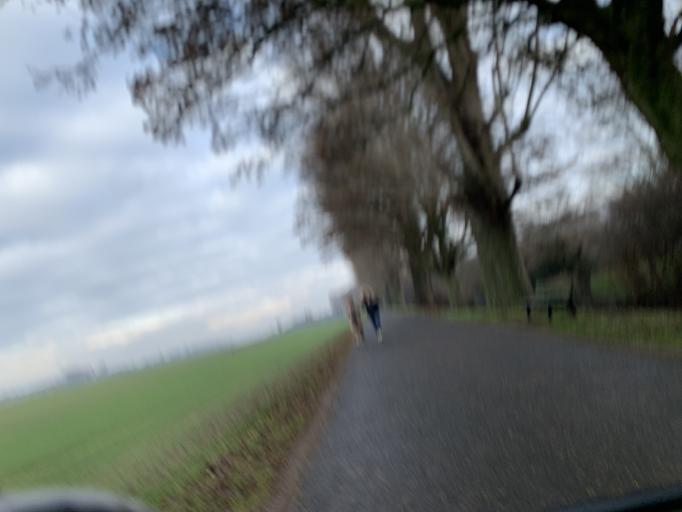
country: DE
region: North Rhine-Westphalia
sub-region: Regierungsbezirk Dusseldorf
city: Meerbusch
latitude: 51.2848
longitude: 6.7228
